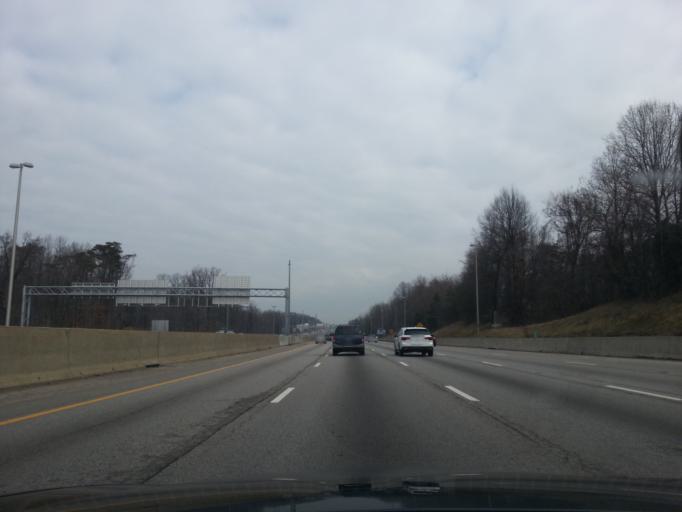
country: US
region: Virginia
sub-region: Fairfax County
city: Lorton
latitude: 38.6867
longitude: -77.2275
